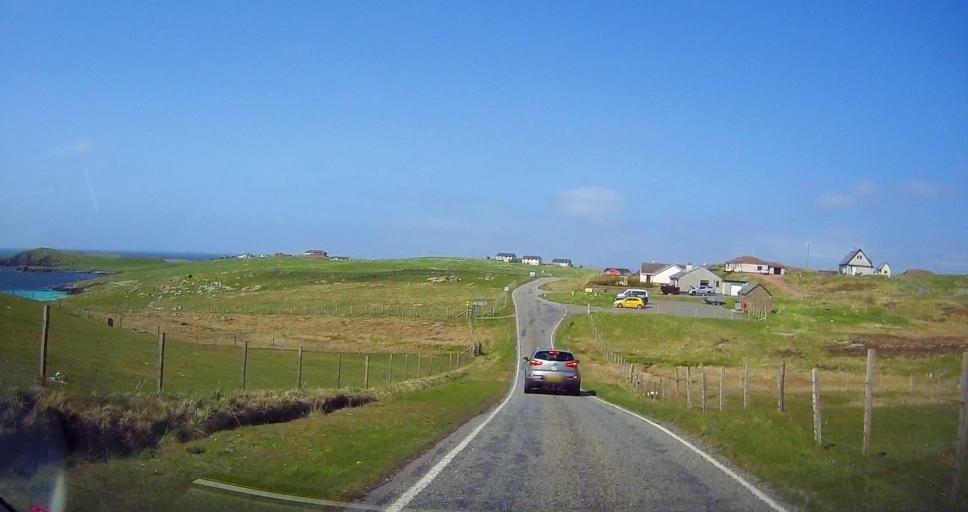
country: GB
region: Scotland
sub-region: Shetland Islands
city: Sandwick
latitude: 60.1014
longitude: -1.3222
